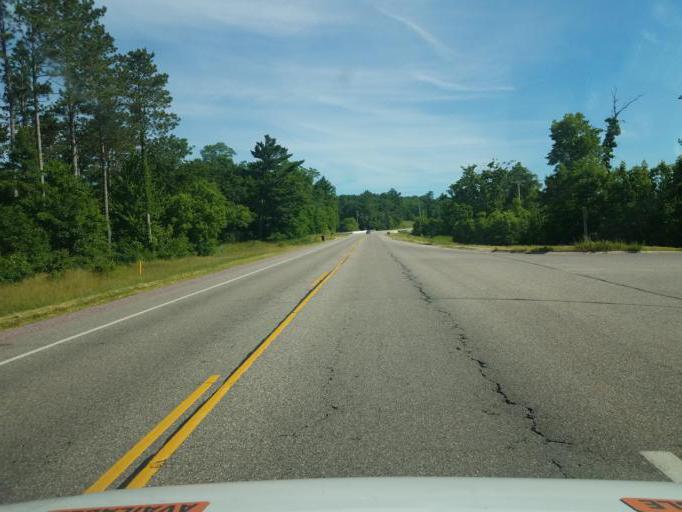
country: US
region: Wisconsin
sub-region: Sauk County
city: Lake Delton
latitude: 43.5570
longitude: -89.8422
